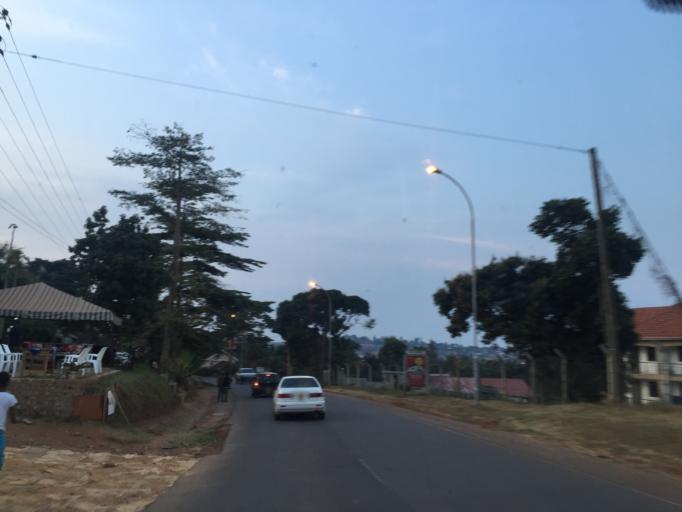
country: UG
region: Central Region
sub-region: Kampala District
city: Kampala
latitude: 0.2452
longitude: 32.6282
